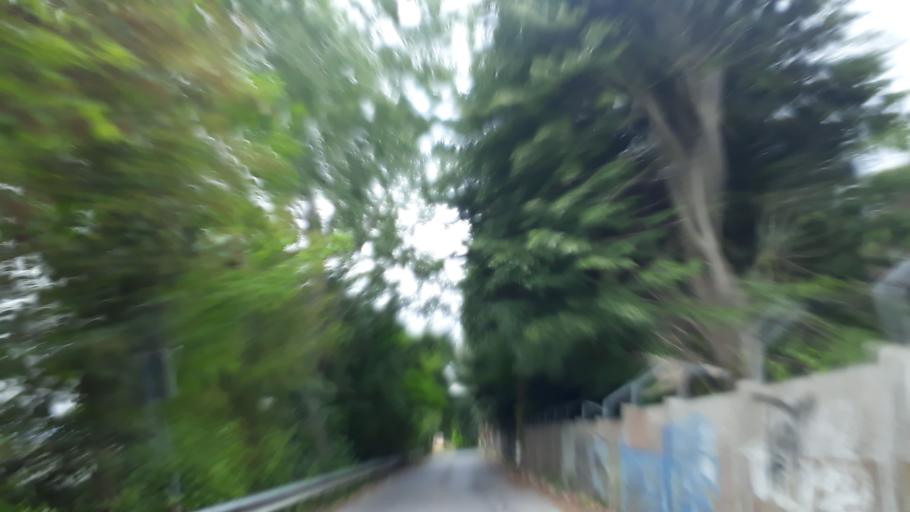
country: FR
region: Ile-de-France
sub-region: Departement de l'Essonne
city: La Ville-du-Bois
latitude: 48.6686
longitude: 2.2723
